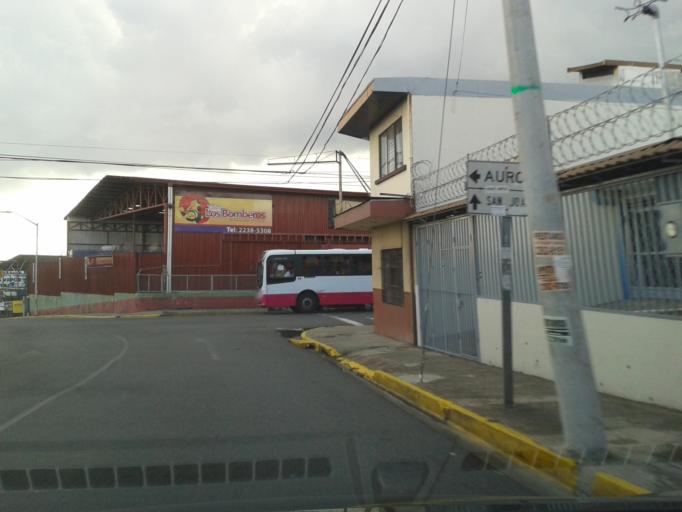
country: CR
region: Heredia
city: San Francisco
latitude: 9.9977
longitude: -84.1231
